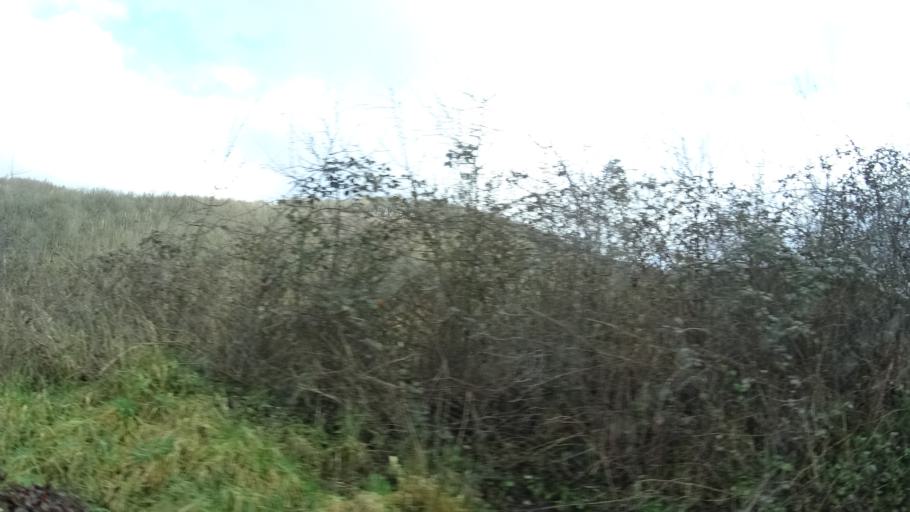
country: DE
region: Rheinland-Pfalz
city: Wurzweiler
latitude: 49.6546
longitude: 7.8663
